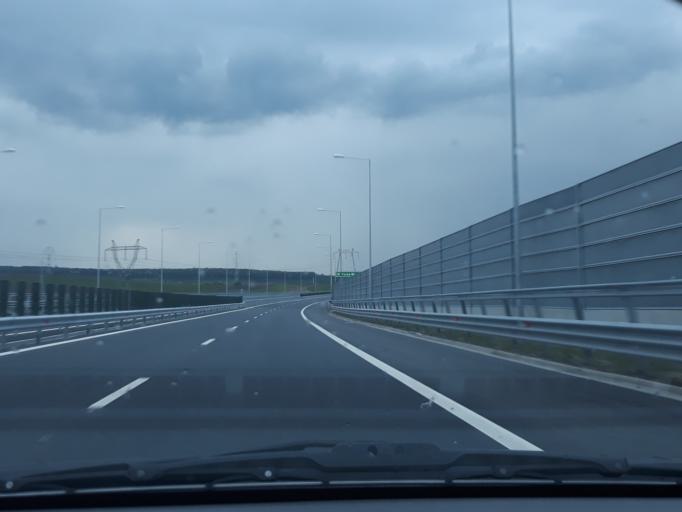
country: RO
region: Mures
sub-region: Comuna Sanpaul
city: Valea Izvoarelor
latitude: 46.4514
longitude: 24.3760
